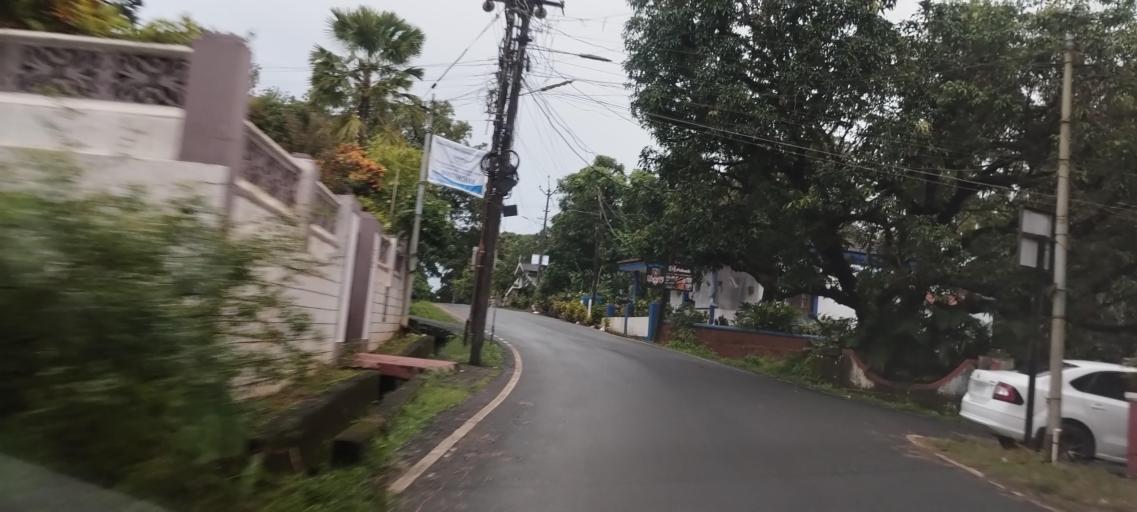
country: IN
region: Goa
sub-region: North Goa
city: Jua
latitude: 15.5250
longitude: 73.9026
